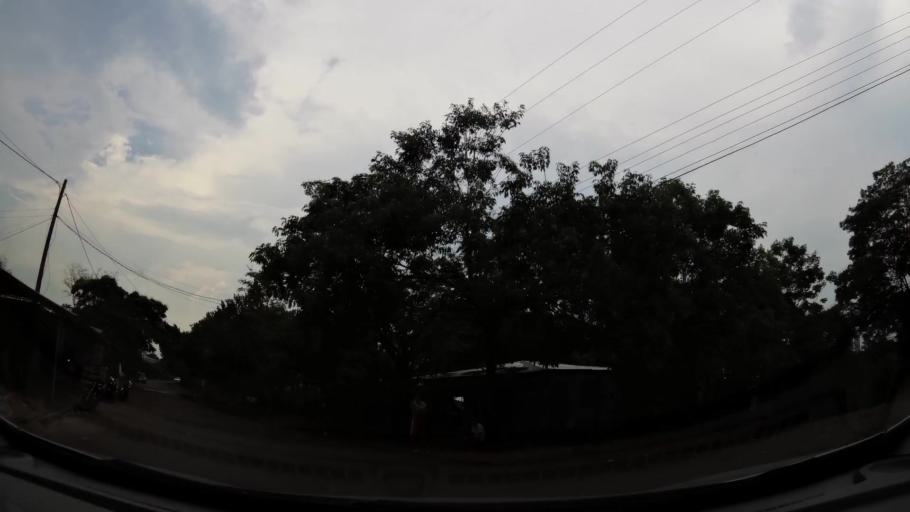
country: BR
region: Parana
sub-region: Foz Do Iguacu
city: Foz do Iguacu
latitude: -25.5476
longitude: -54.5979
